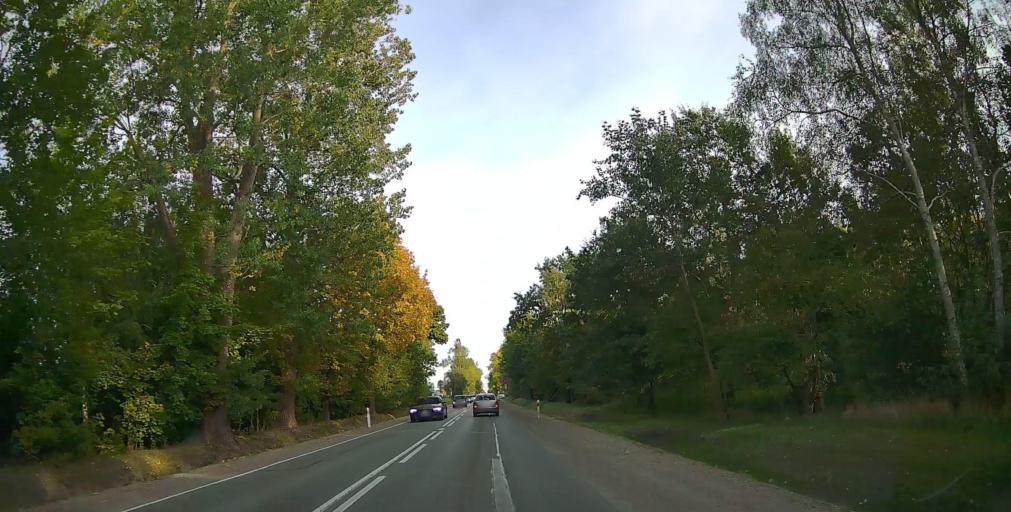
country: PL
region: Masovian Voivodeship
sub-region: Powiat piaseczynski
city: Zabieniec
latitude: 52.0570
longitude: 21.0511
